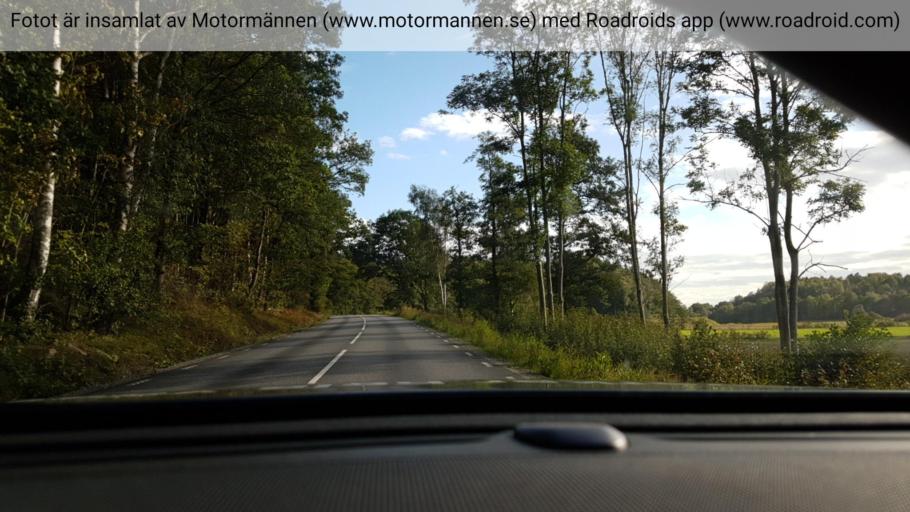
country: SE
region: Vaestra Goetaland
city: Svanesund
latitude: 58.1172
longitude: 11.8544
